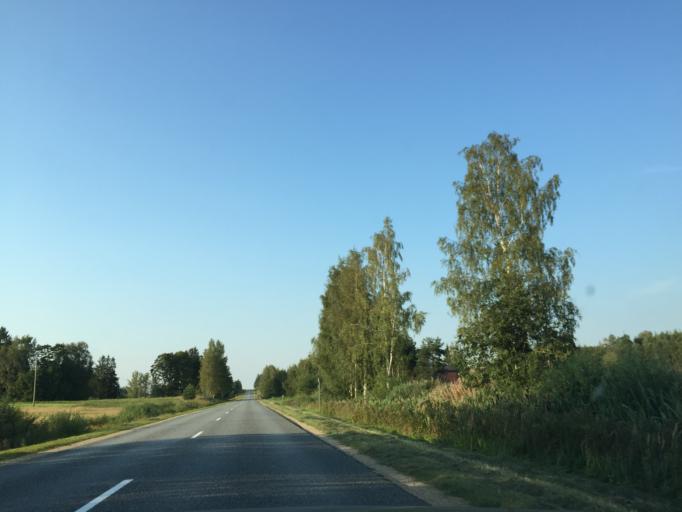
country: LV
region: Limbazu Rajons
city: Limbazi
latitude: 57.5643
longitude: 24.7669
